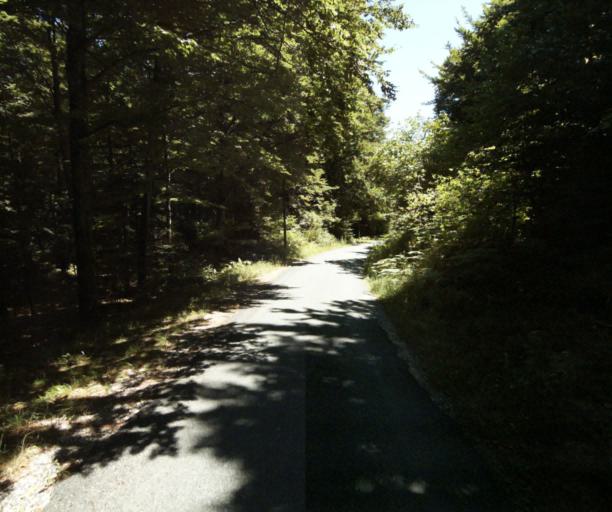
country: FR
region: Languedoc-Roussillon
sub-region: Departement de l'Aude
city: Cuxac-Cabardes
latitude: 43.4000
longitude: 2.2186
